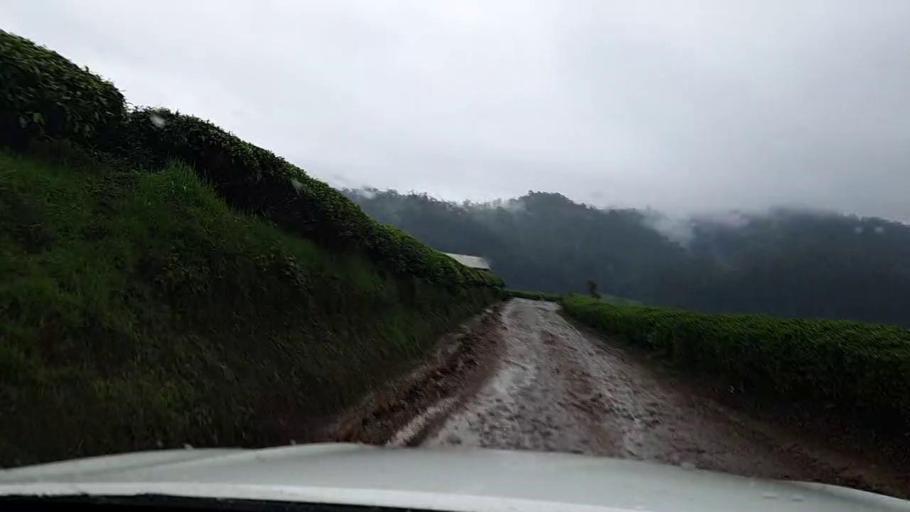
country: RW
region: Western Province
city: Cyangugu
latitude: -2.4575
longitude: 29.0381
